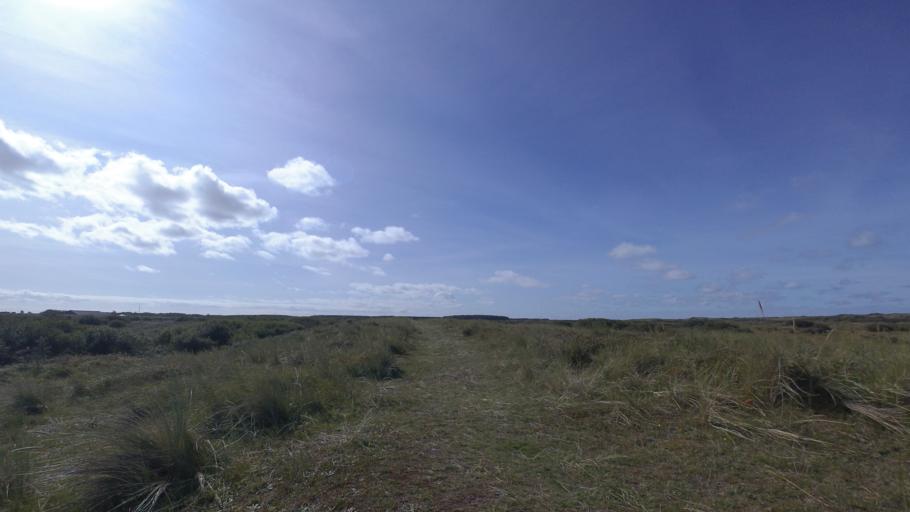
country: NL
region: Friesland
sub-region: Gemeente Ameland
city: Nes
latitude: 53.4548
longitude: 5.7366
